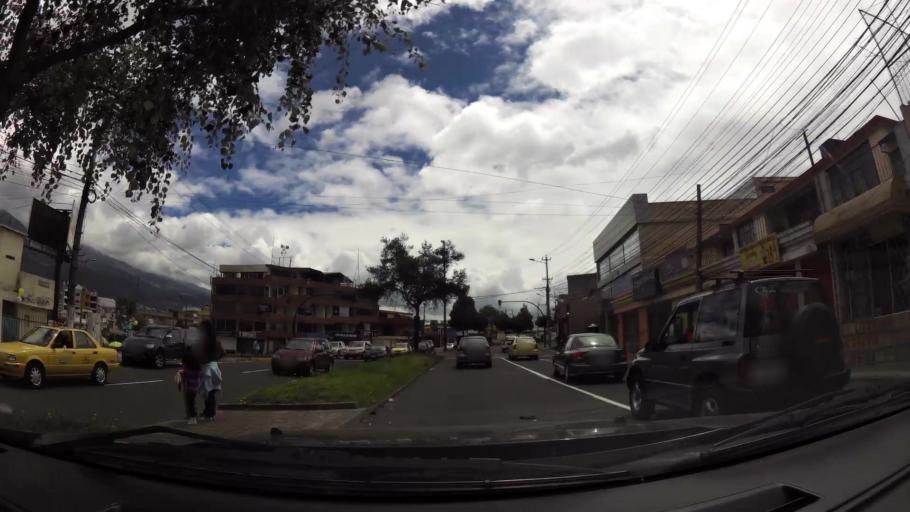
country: EC
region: Pichincha
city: Quito
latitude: -0.1600
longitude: -78.4770
